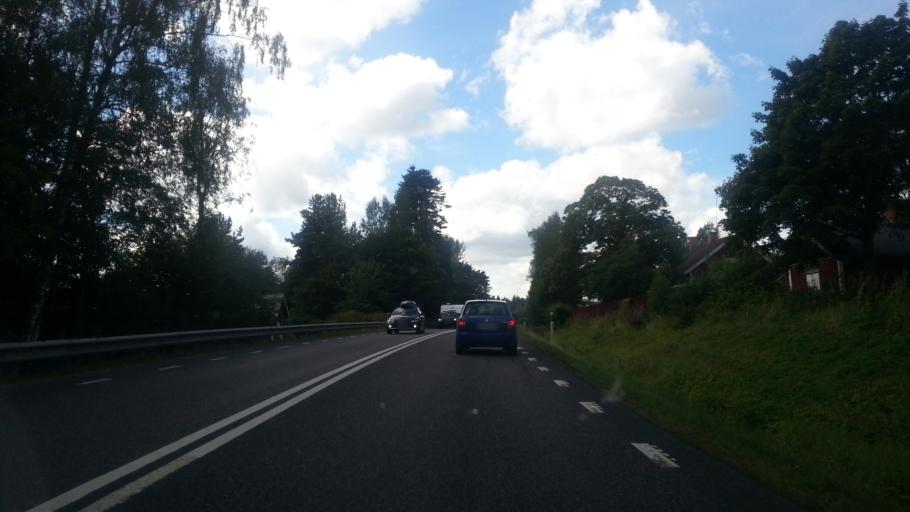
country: SE
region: Dalarna
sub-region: Ludvika Kommun
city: Ludvika
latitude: 60.1058
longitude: 15.1036
